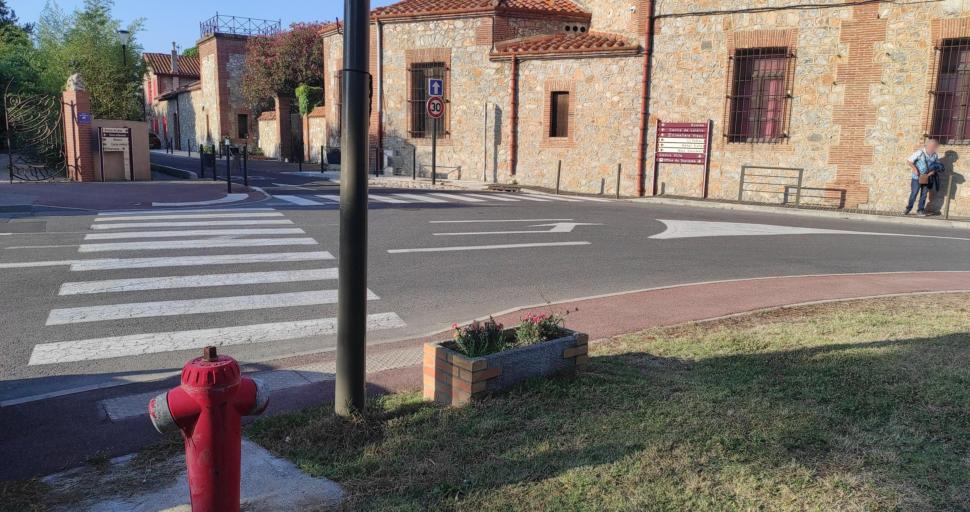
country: FR
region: Languedoc-Roussillon
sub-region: Departement des Pyrenees-Orientales
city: Alenya
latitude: 42.6395
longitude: 2.9800
